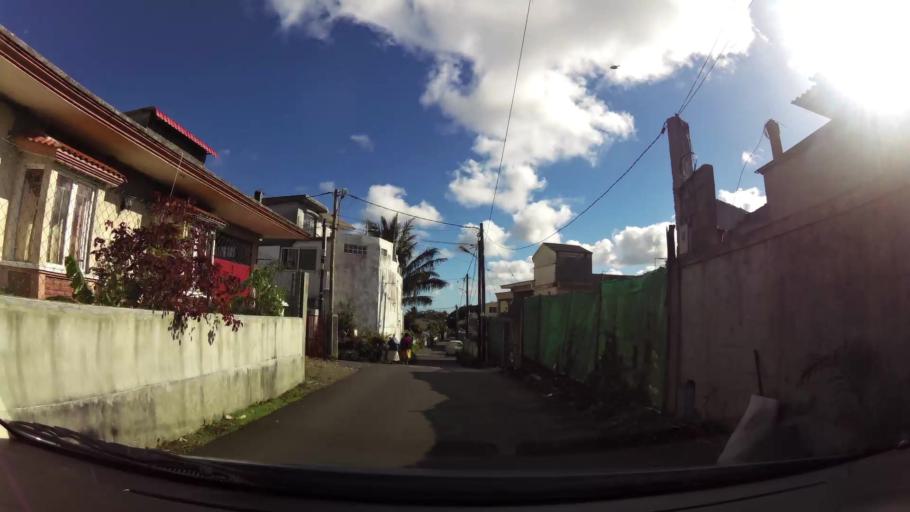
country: MU
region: Plaines Wilhems
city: Curepipe
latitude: -20.3015
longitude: 57.5180
